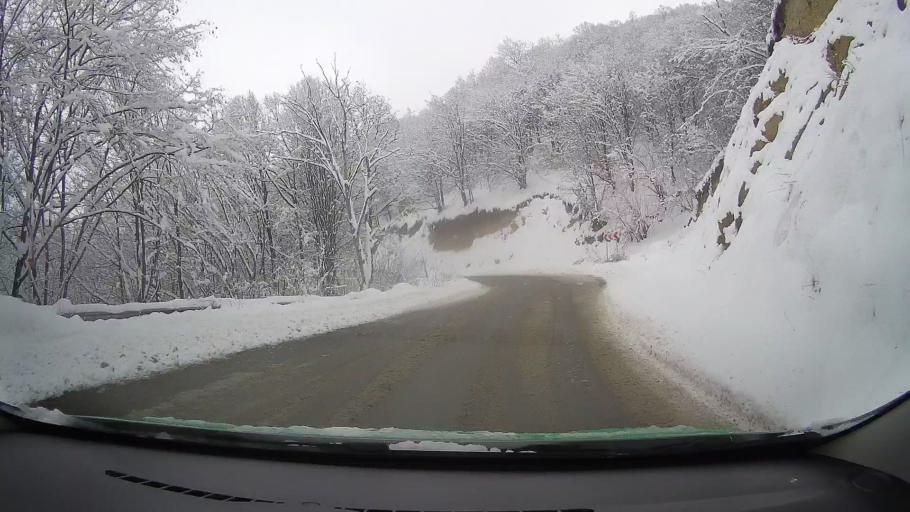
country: RO
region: Sibiu
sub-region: Comuna Jina
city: Jina
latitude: 45.7682
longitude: 23.6700
